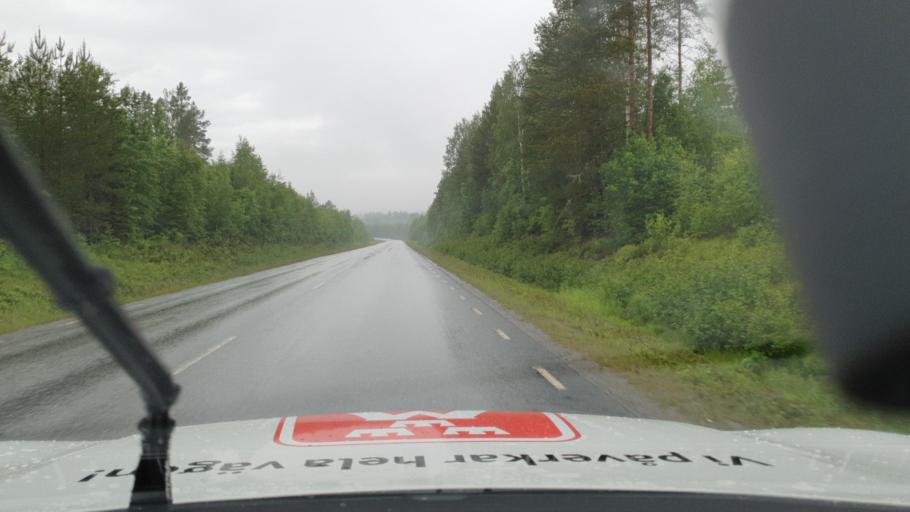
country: SE
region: Vaesterbotten
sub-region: Umea Kommun
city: Roback
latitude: 63.7855
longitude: 20.1061
